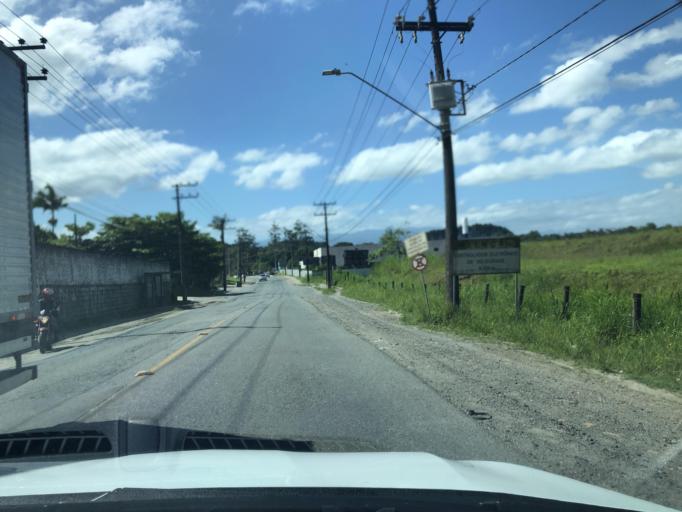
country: BR
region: Santa Catarina
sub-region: Joinville
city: Joinville
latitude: -26.2565
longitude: -48.8690
